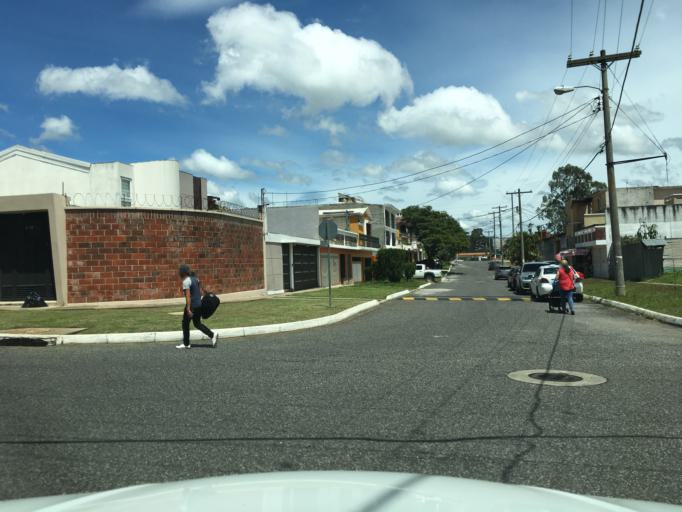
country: GT
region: Guatemala
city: Mixco
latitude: 14.6577
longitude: -90.5650
